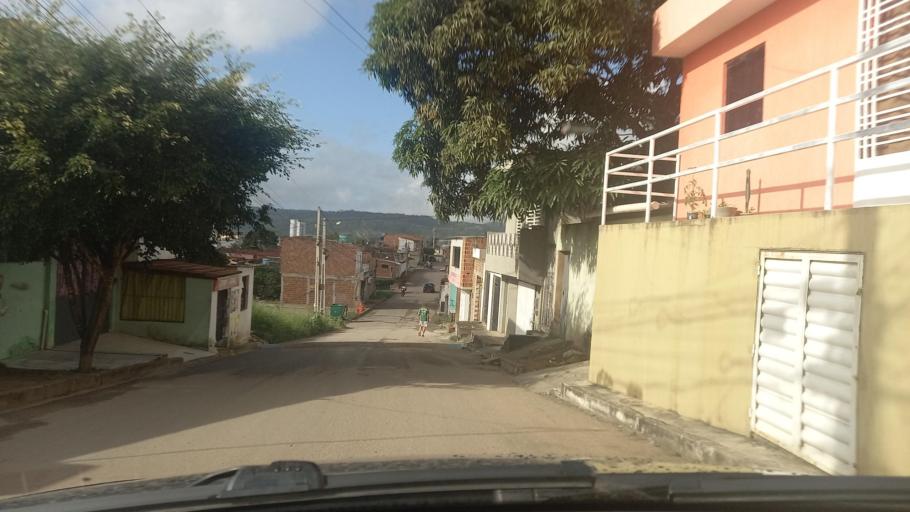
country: BR
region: Pernambuco
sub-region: Vitoria De Santo Antao
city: Vitoria de Santo Antao
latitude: -8.1143
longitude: -35.3075
